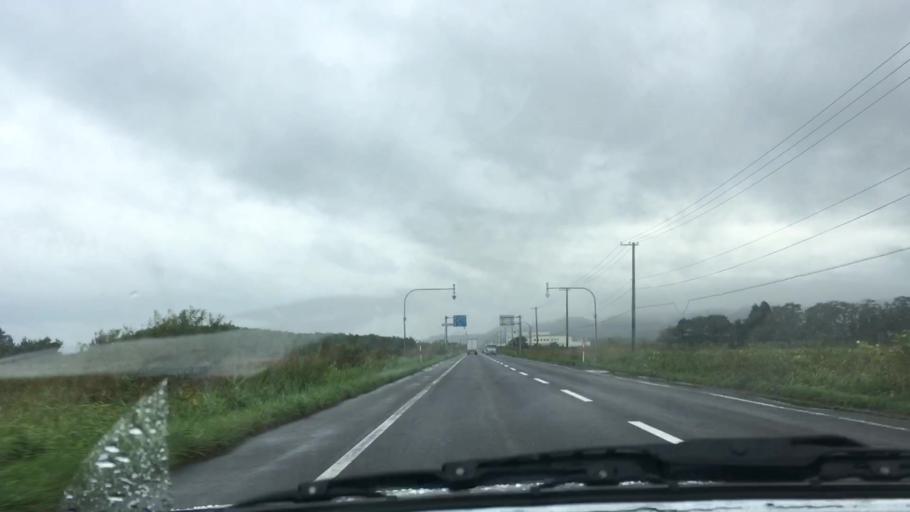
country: JP
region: Hokkaido
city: Niseko Town
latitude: 42.3935
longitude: 140.2997
